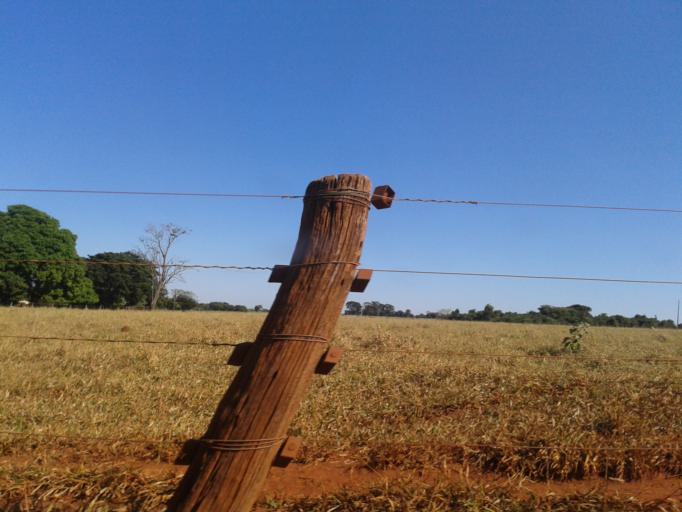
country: BR
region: Minas Gerais
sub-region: Centralina
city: Centralina
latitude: -18.7314
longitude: -49.1779
